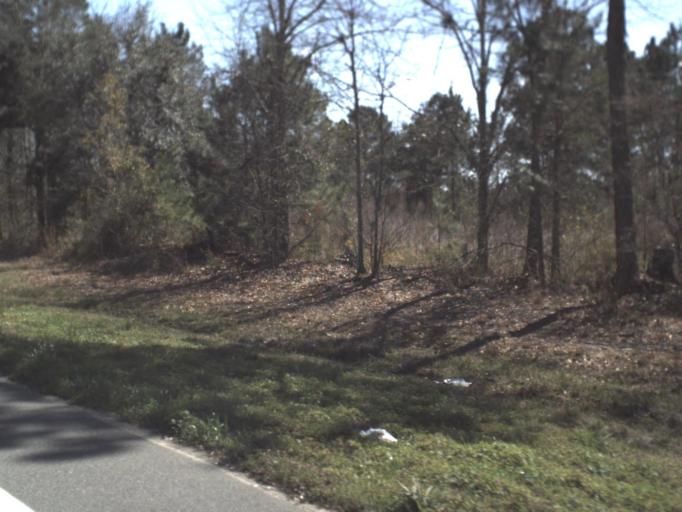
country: US
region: Florida
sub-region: Gadsden County
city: Gretna
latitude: 30.6505
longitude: -84.6824
